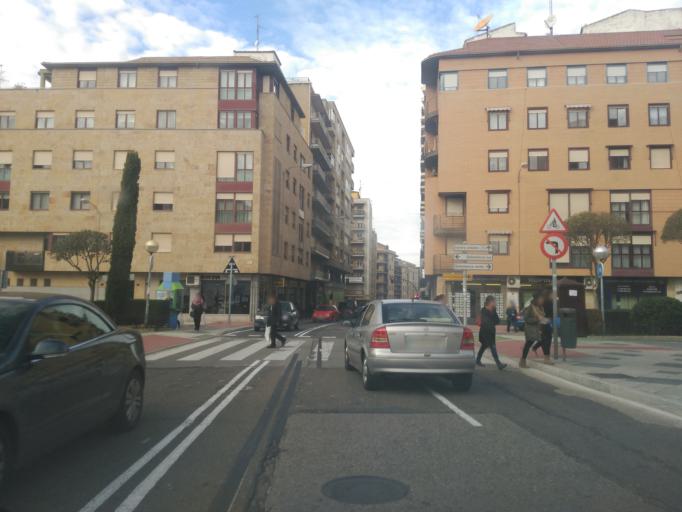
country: ES
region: Castille and Leon
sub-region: Provincia de Salamanca
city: Salamanca
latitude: 40.9647
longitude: -5.6569
